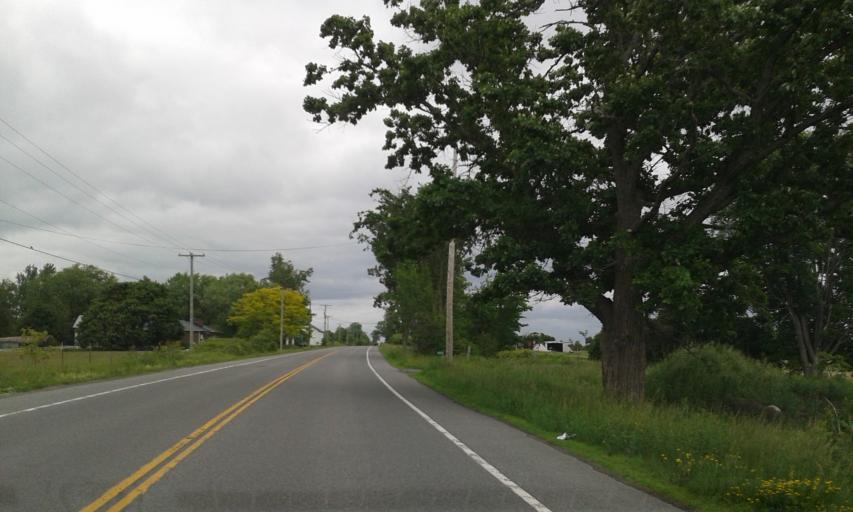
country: CA
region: Ontario
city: Napanee Downtown
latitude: 44.1158
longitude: -76.9109
